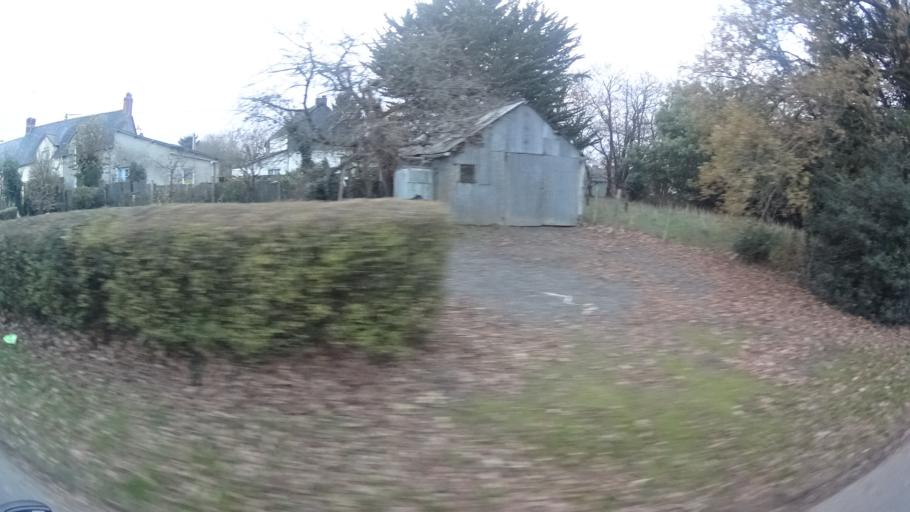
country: FR
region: Pays de la Loire
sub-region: Departement de la Loire-Atlantique
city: Avessac
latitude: 47.6502
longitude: -1.9935
